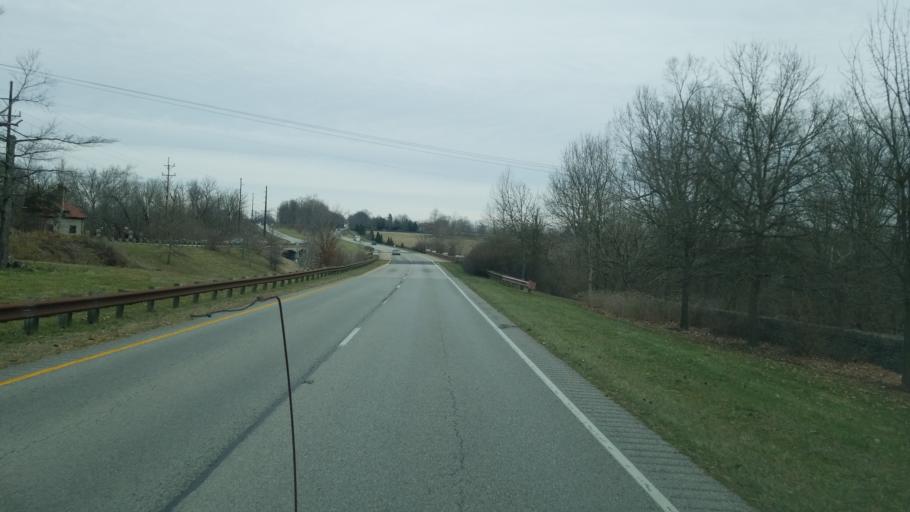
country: US
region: Kentucky
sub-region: Fayette County
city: Lexington-Fayette
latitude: 38.1063
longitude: -84.4085
